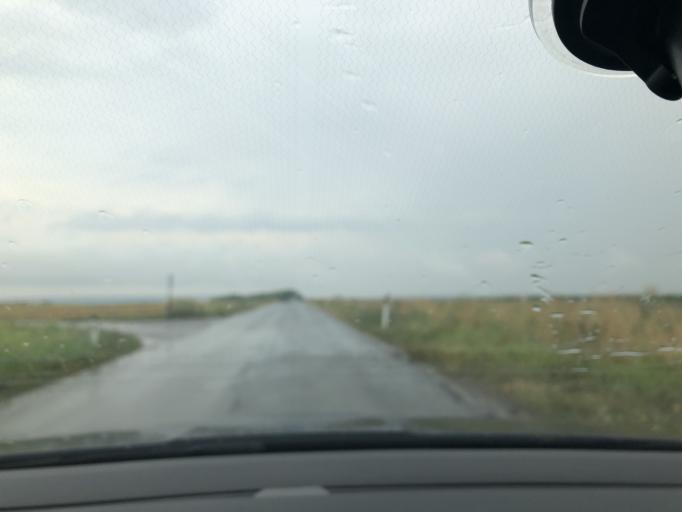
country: AT
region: Lower Austria
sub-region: Politischer Bezirk Ganserndorf
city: Auersthal
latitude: 48.3765
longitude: 16.6446
